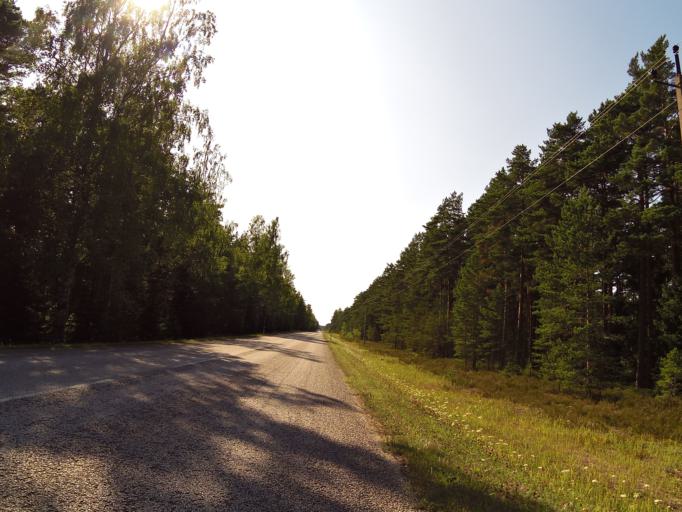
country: EE
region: Hiiumaa
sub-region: Kaerdla linn
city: Kardla
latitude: 58.9113
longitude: 22.3559
